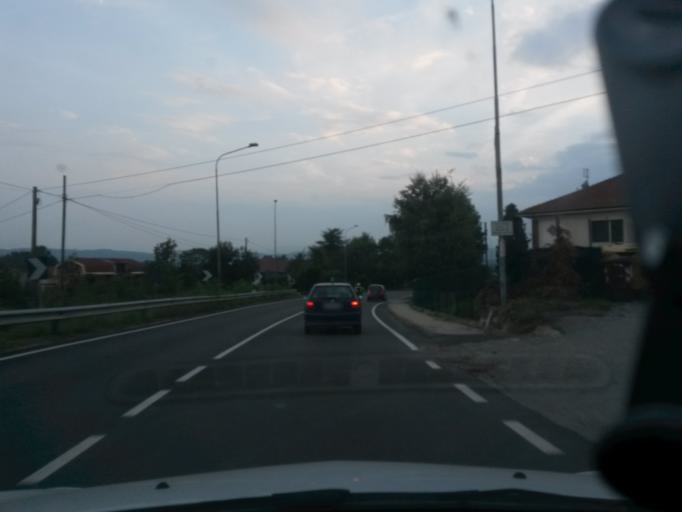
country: IT
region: Piedmont
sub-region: Provincia di Torino
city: Caselette
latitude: 45.1019
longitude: 7.4735
